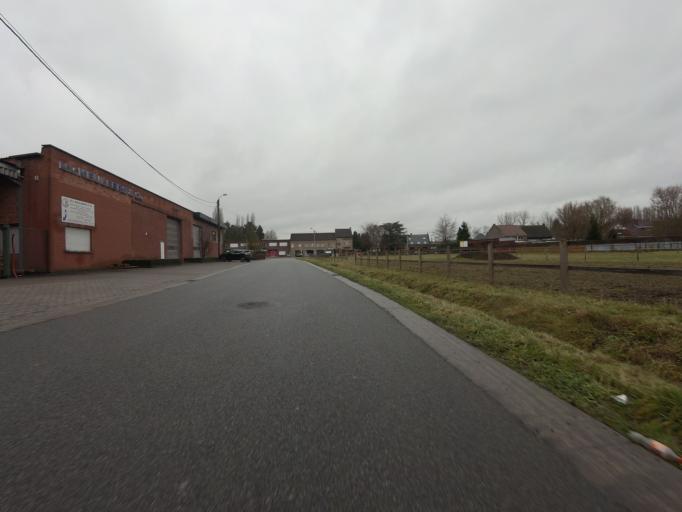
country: BE
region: Flanders
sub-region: Provincie Antwerpen
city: Sint-Katelijne-Waver
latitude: 51.0449
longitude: 4.5248
